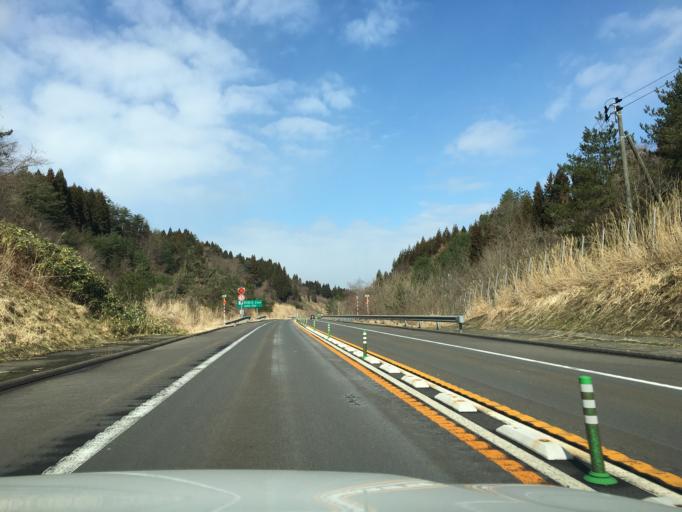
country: JP
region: Akita
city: Akita
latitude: 39.7642
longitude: 140.1258
